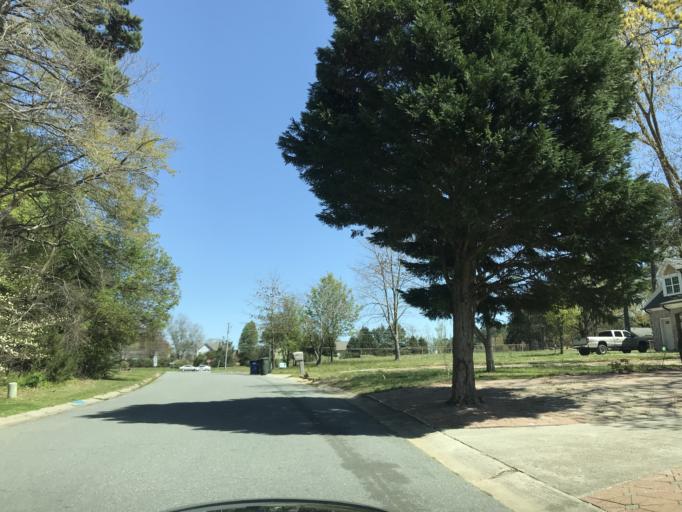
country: US
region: North Carolina
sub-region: Wake County
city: Raleigh
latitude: 35.8150
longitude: -78.5687
